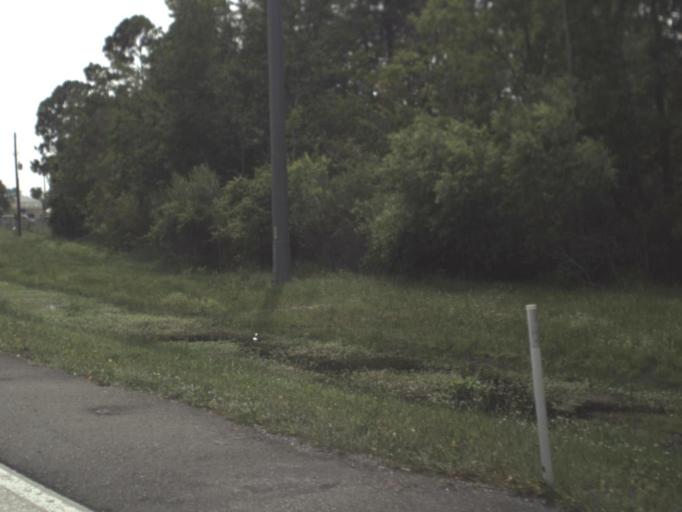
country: US
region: Florida
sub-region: Duval County
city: Jacksonville
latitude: 30.4047
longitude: -81.6598
